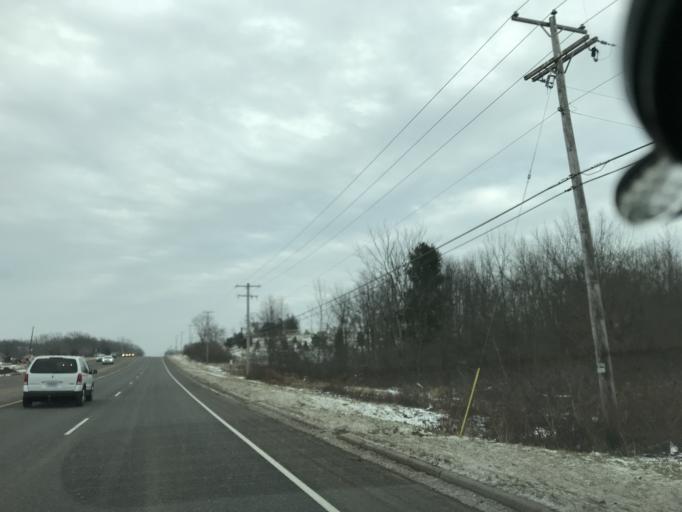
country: US
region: Michigan
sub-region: Kent County
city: Rockford
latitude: 43.1170
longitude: -85.5937
